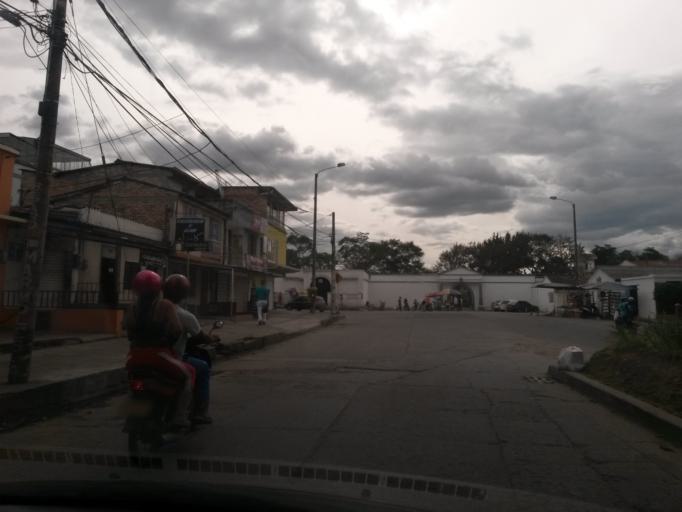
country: CO
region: Cauca
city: Popayan
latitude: 2.4475
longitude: -76.6195
